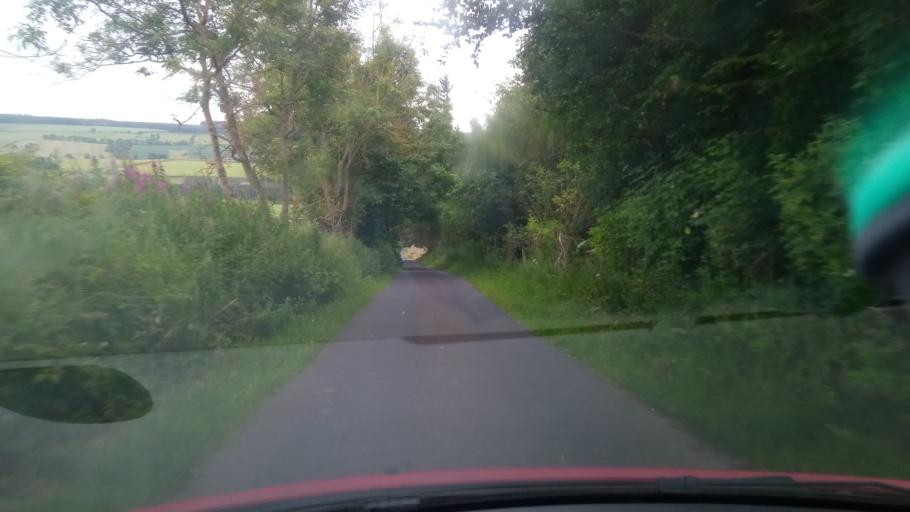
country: GB
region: Scotland
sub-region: The Scottish Borders
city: Saint Boswells
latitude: 55.5018
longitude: -2.6231
